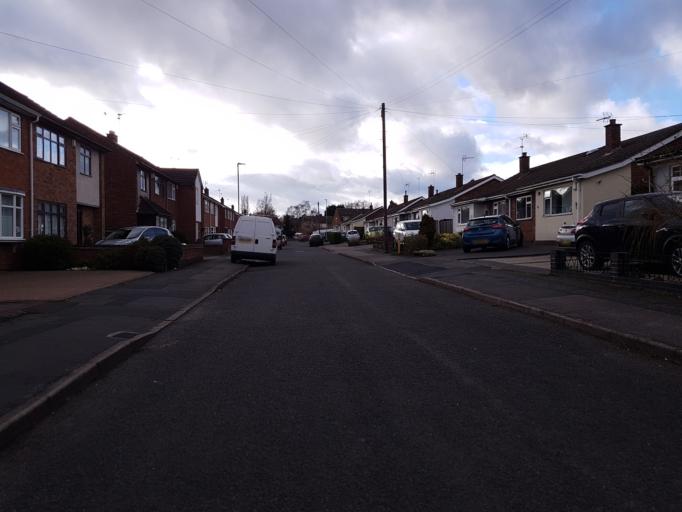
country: GB
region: England
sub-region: Leicestershire
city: Earl Shilton
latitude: 52.5677
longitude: -1.3212
